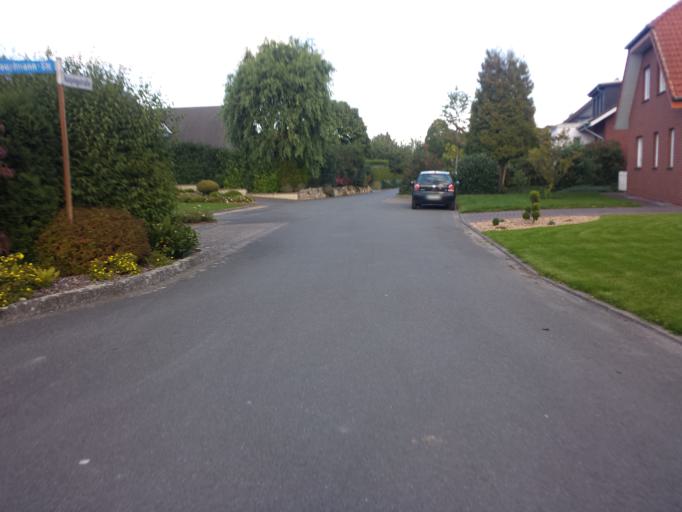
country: DE
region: North Rhine-Westphalia
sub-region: Regierungsbezirk Detmold
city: Langenberg
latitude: 51.7477
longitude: 8.3225
